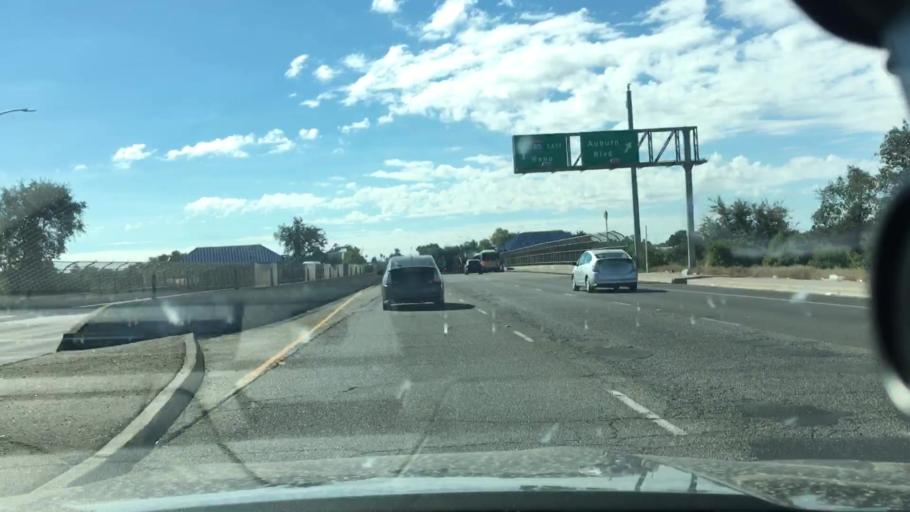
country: US
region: California
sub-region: Sacramento County
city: North Highlands
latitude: 38.6464
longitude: -121.3833
